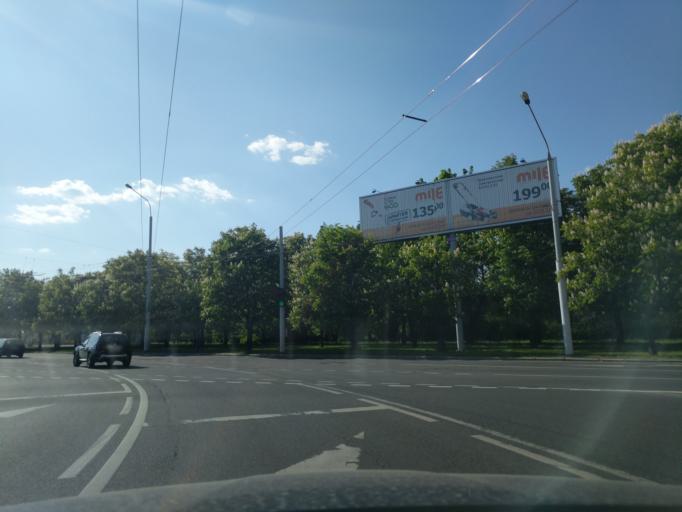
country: BY
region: Minsk
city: Minsk
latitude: 53.9316
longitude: 27.5774
